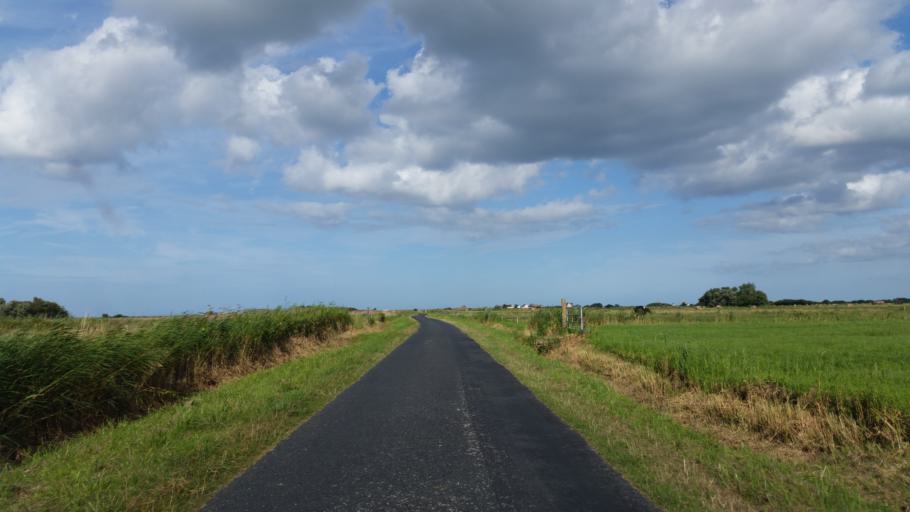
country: FR
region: Lower Normandy
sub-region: Departement de la Manche
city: Sainte-Mere-Eglise
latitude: 49.4527
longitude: -1.2435
